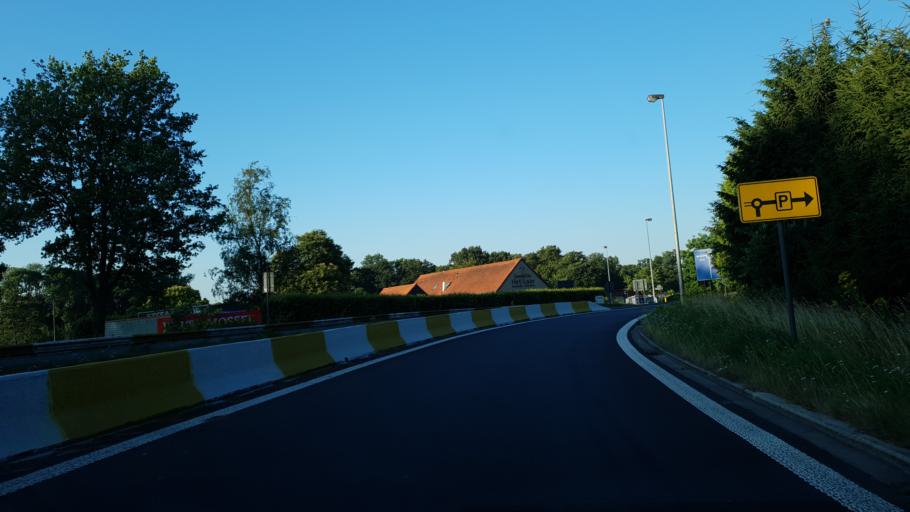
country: BE
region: Flanders
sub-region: Provincie Antwerpen
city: Beerse
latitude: 51.2849
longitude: 4.8577
